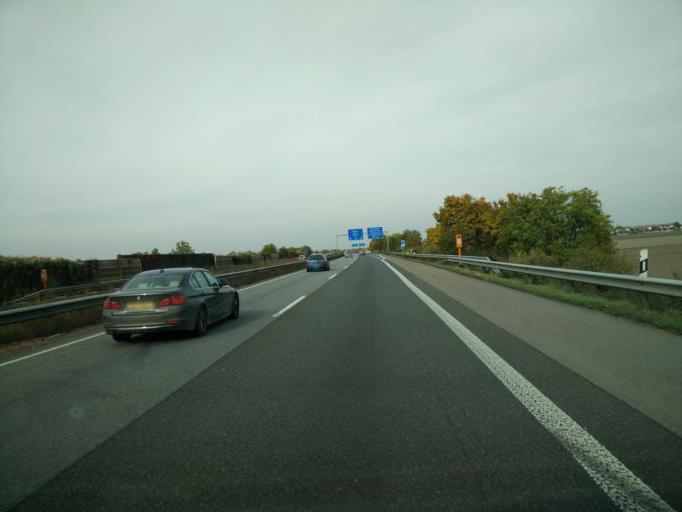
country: DE
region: Rheinland-Pfalz
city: Hessheim
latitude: 49.5463
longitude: 8.3159
